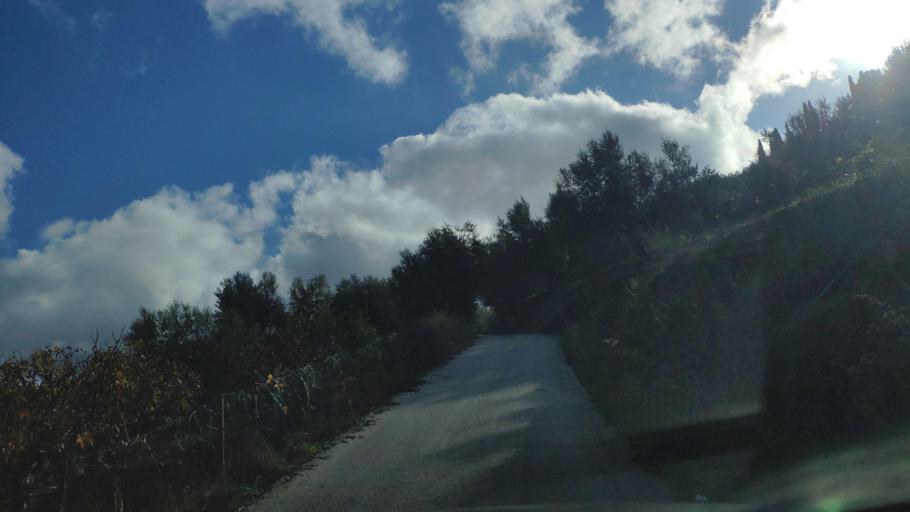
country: GR
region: West Greece
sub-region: Nomos Achaias
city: Aiyira
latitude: 38.1052
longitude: 22.4438
